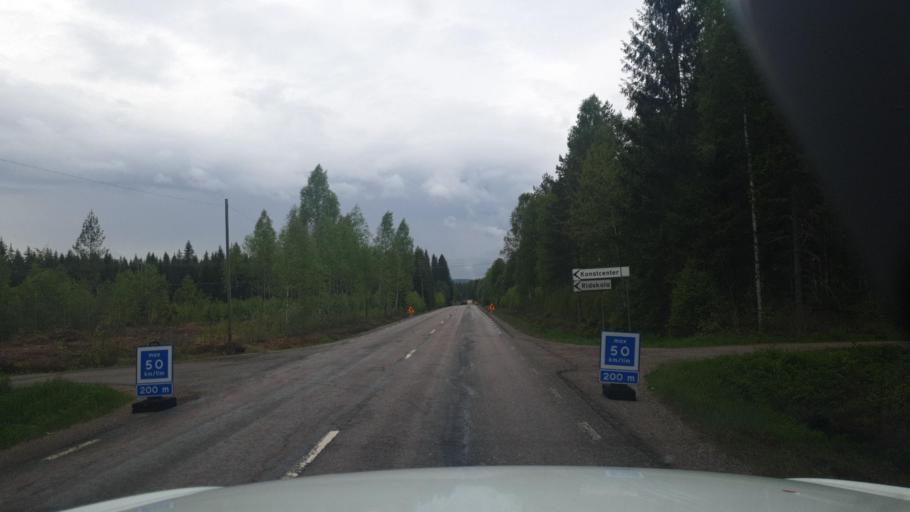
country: SE
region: Vaermland
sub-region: Eda Kommun
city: Charlottenberg
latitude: 59.8478
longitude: 12.3024
